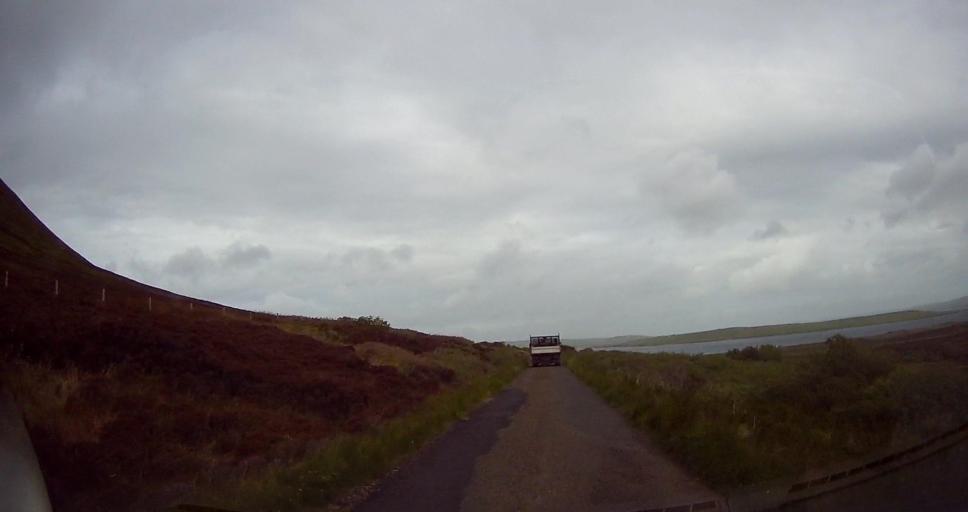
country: GB
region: Scotland
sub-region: Orkney Islands
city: Stromness
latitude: 58.8969
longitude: -3.3146
